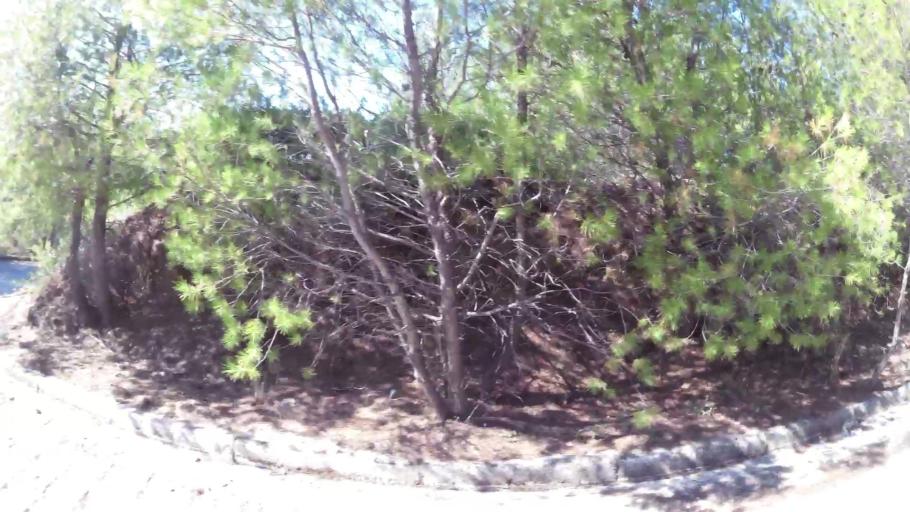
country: GR
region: Attica
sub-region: Nomarchia Anatolikis Attikis
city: Dioni
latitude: 38.0234
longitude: 23.9313
